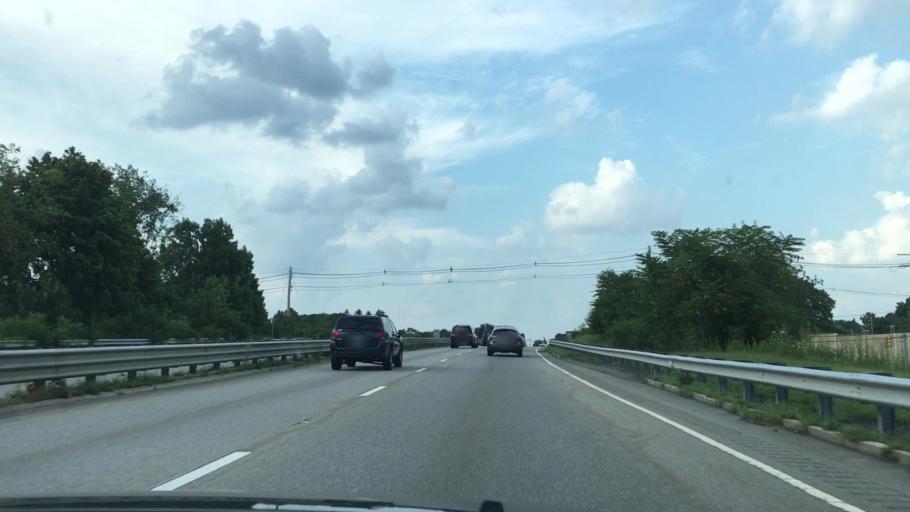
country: US
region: Massachusetts
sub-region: Essex County
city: Danvers
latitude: 42.5644
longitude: -70.9236
